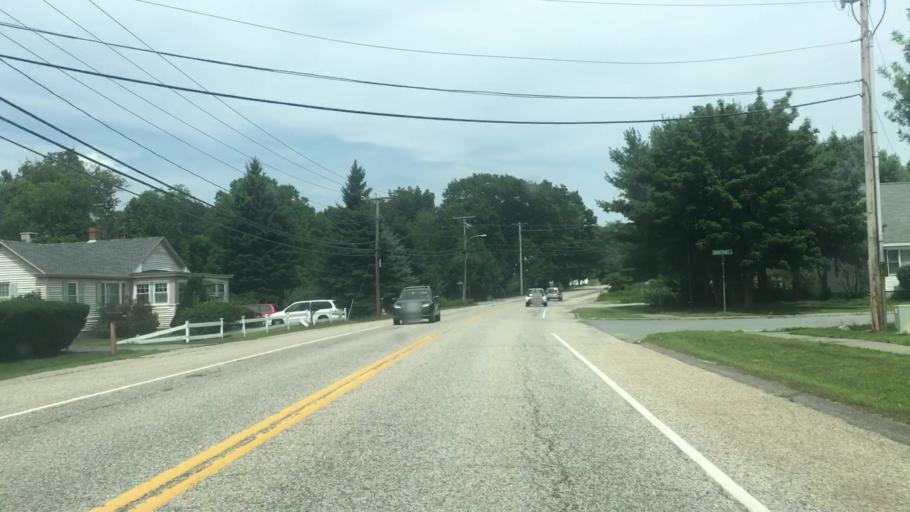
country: US
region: Maine
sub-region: Cumberland County
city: South Portland Gardens
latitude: 43.6076
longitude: -70.2832
